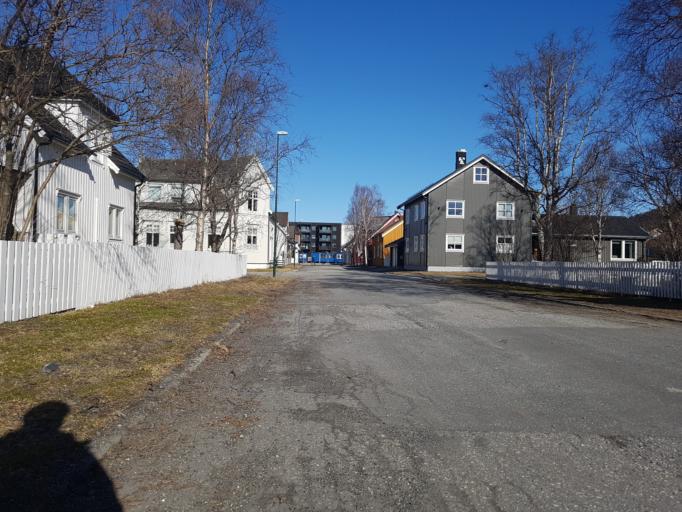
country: NO
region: Nordland
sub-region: Vefsn
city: Mosjoen
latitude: 65.8386
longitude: 13.1978
